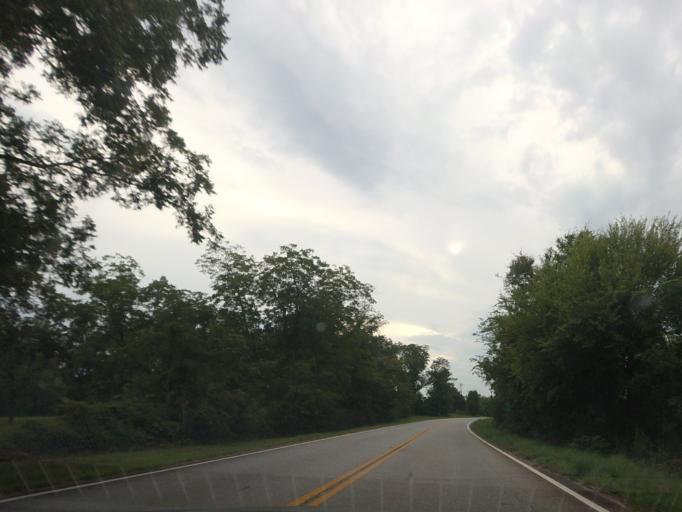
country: US
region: Georgia
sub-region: Twiggs County
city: Jeffersonville
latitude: 32.7487
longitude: -83.4375
